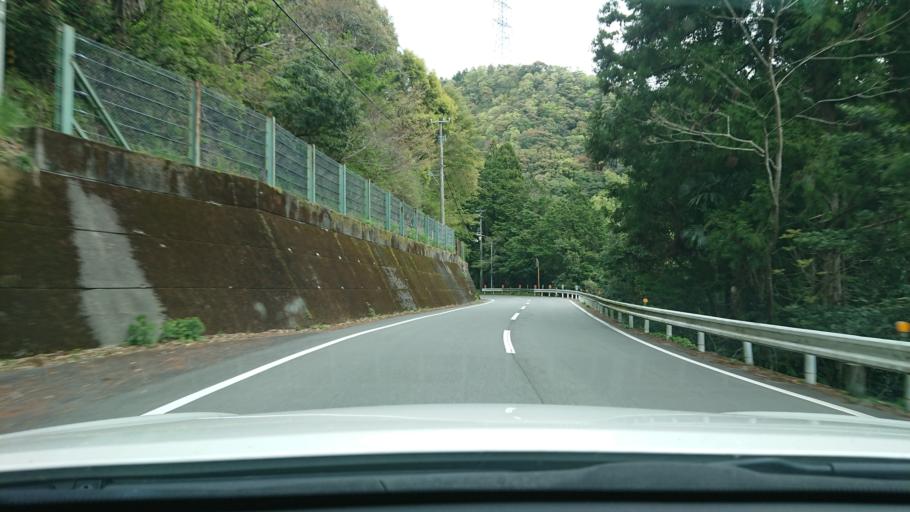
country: JP
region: Tokushima
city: Ishii
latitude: 33.9096
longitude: 134.4208
